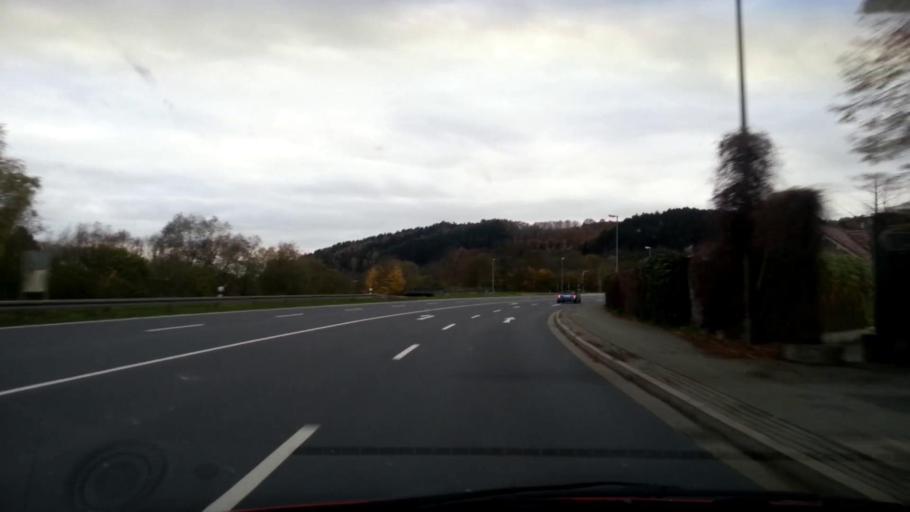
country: DE
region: Bavaria
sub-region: Upper Franconia
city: Kronach
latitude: 50.2294
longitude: 11.3209
